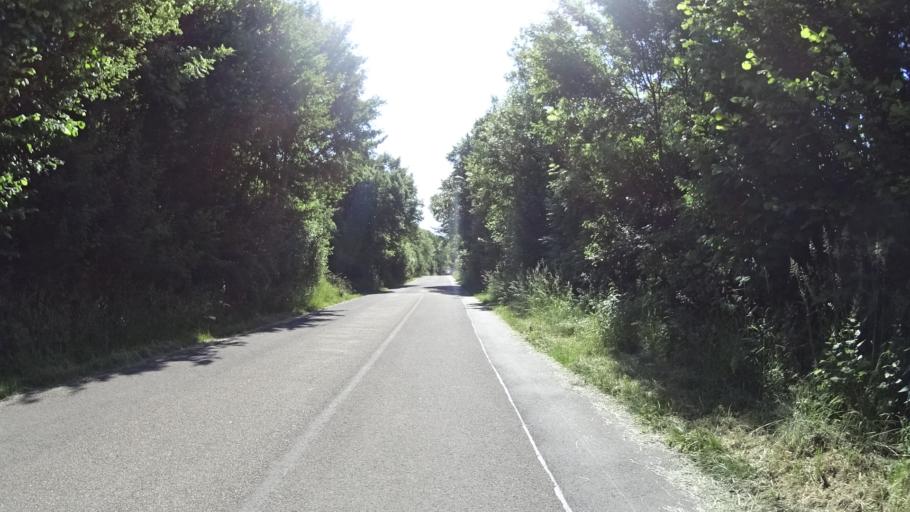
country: DE
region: Baden-Wuerttemberg
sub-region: Regierungsbezirk Stuttgart
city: Bad Mergentheim
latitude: 49.4995
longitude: 9.7630
